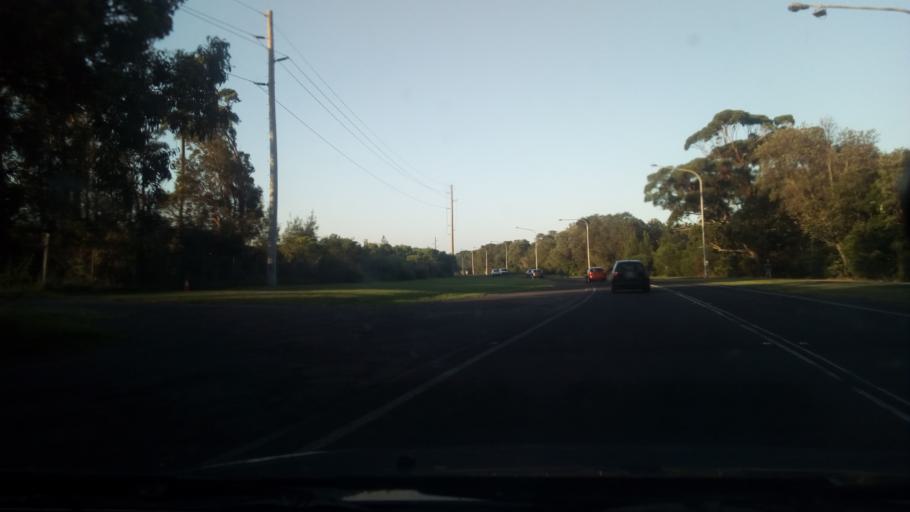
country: AU
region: New South Wales
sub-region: Wollongong
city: Fairy Meadow
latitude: -34.4063
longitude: 150.8992
